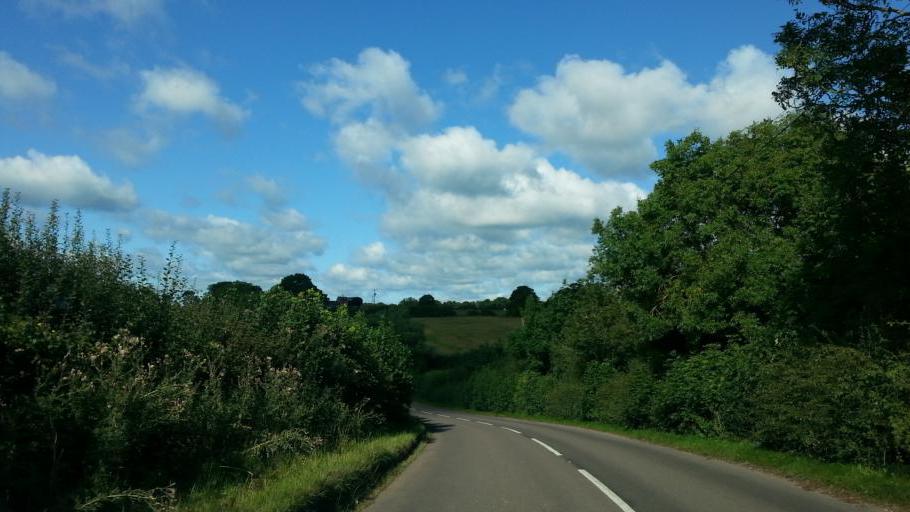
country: GB
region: England
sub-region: Staffordshire
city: Uttoxeter
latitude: 52.8268
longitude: -1.8084
